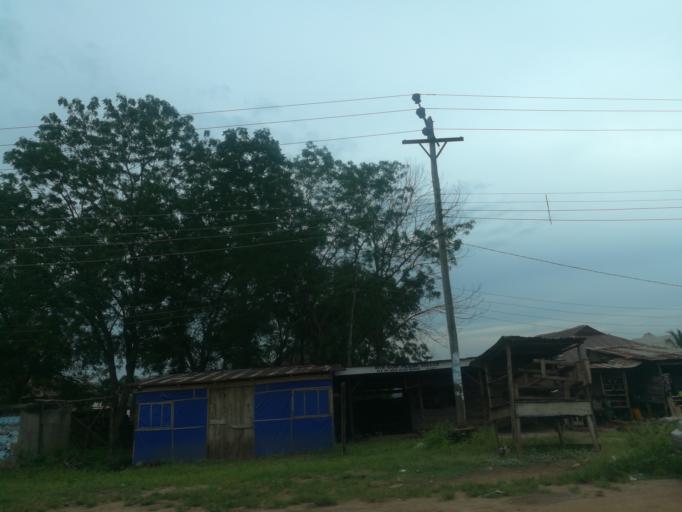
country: NG
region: Oyo
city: Egbeda
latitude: 7.3855
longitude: 3.9951
